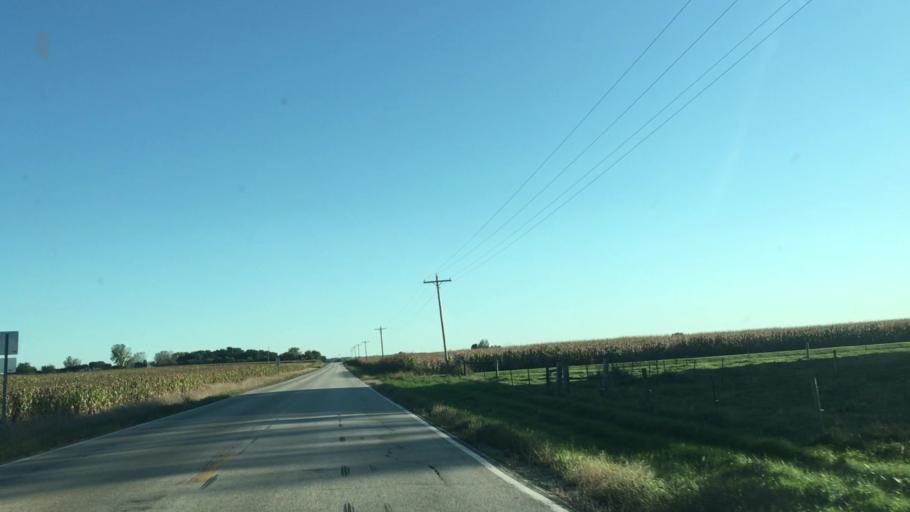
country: US
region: Minnesota
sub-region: Fillmore County
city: Chatfield
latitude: 43.8319
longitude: -92.0694
